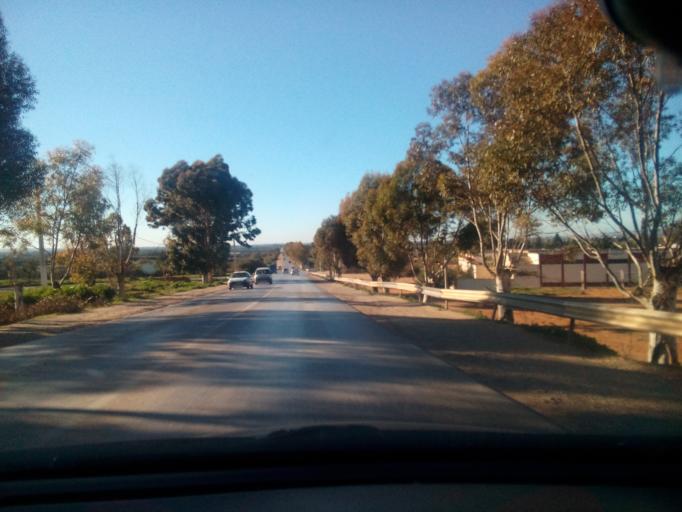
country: DZ
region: Mostaganem
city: Mostaganem
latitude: 35.8970
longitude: 0.2531
